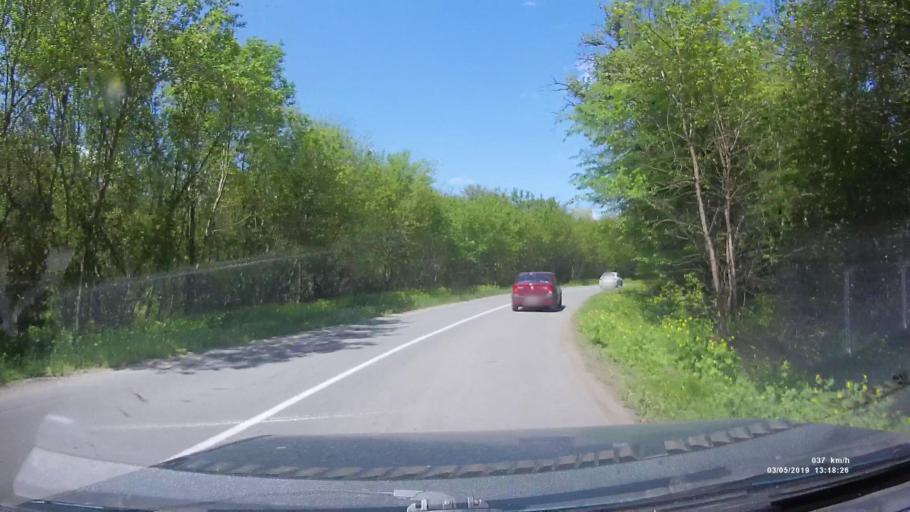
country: RU
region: Rostov
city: Semikarakorsk
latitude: 47.5326
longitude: 40.7483
